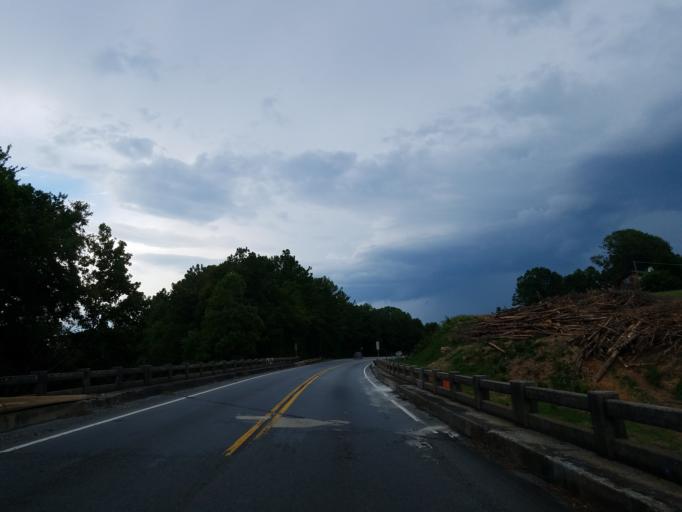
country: US
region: Georgia
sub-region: Bartow County
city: Adairsville
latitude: 34.3201
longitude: -84.8993
